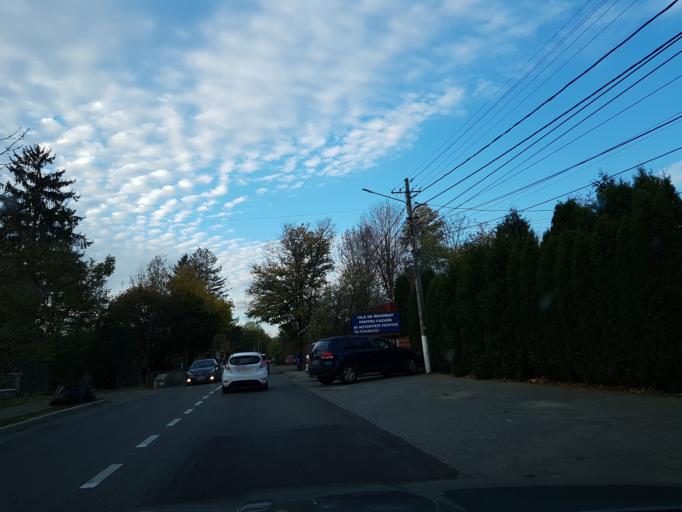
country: RO
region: Prahova
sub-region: Oras Breaza
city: Breaza de Jos
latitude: 45.1711
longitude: 25.6745
